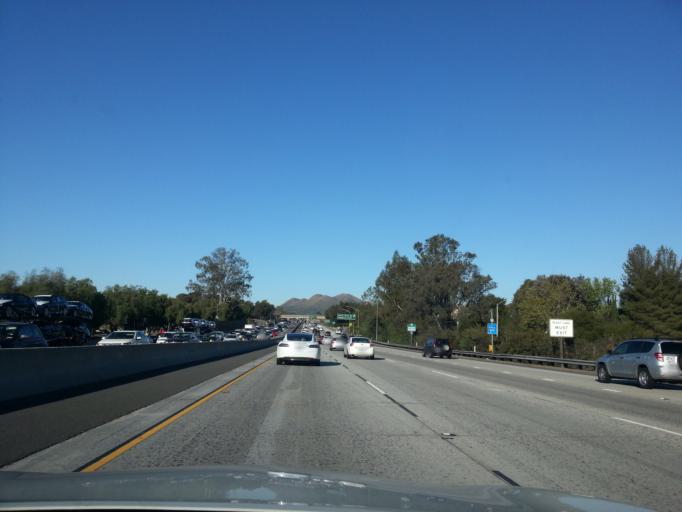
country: US
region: California
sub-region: Ventura County
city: Casa Conejo
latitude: 34.1845
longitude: -118.9044
